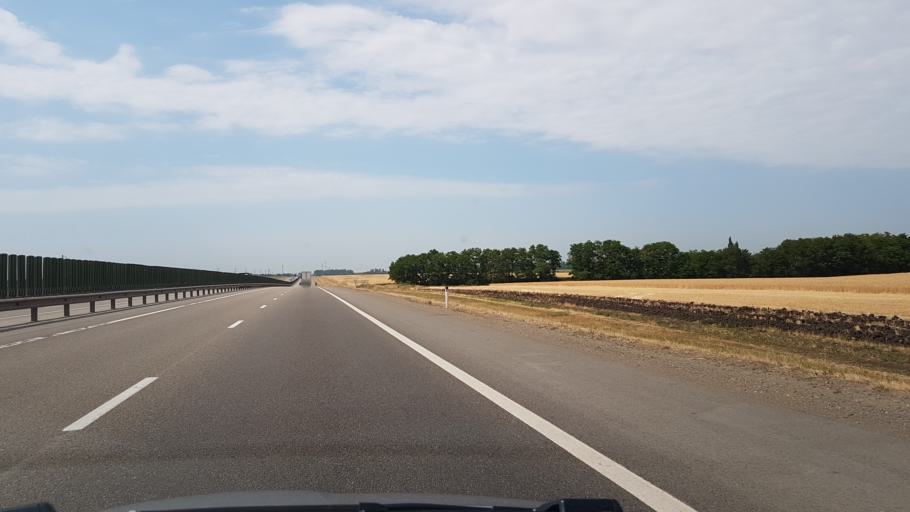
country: RU
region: Krasnodarskiy
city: Plastunovskaya
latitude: 45.2788
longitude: 39.2170
